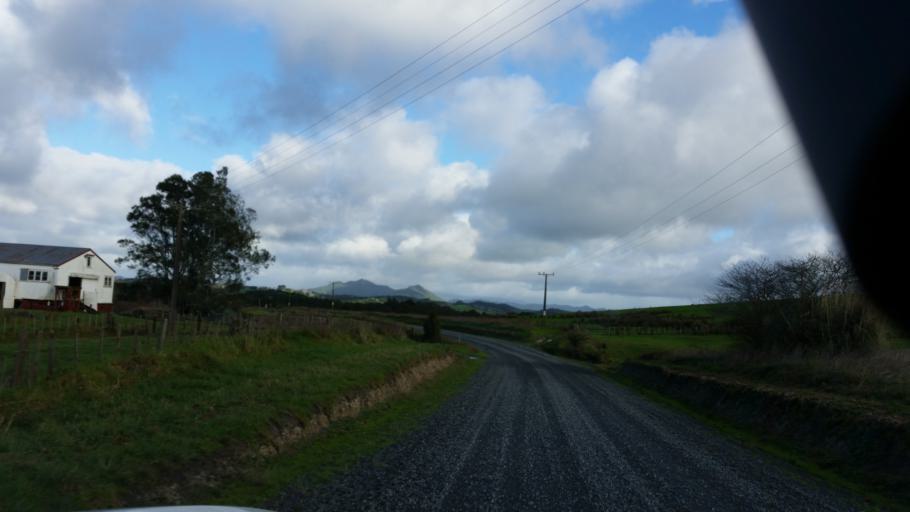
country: NZ
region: Northland
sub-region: Whangarei
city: Maungatapere
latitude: -35.7181
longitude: 174.0741
